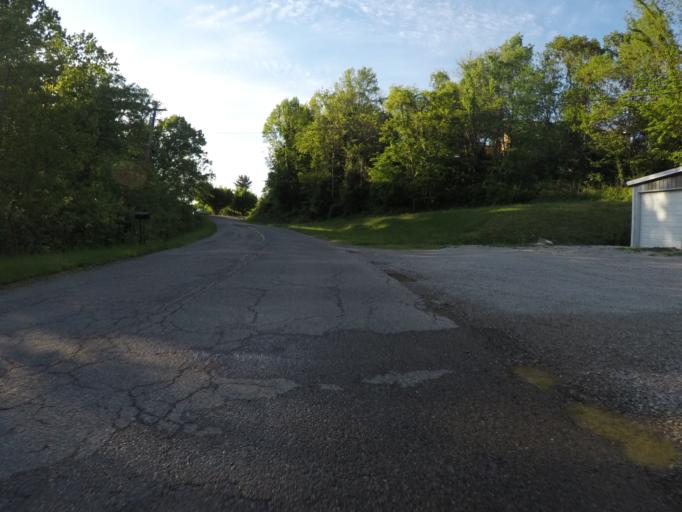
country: US
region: West Virginia
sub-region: Cabell County
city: Huntington
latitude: 38.5519
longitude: -82.4263
